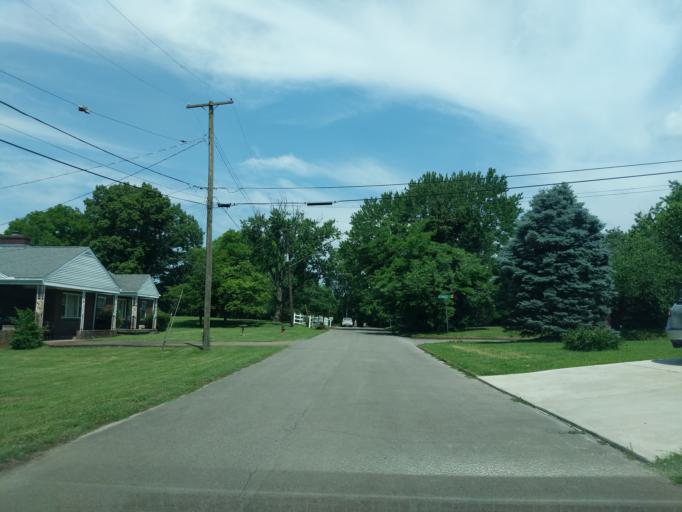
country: US
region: Tennessee
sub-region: Davidson County
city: Lakewood
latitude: 36.2543
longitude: -86.6429
